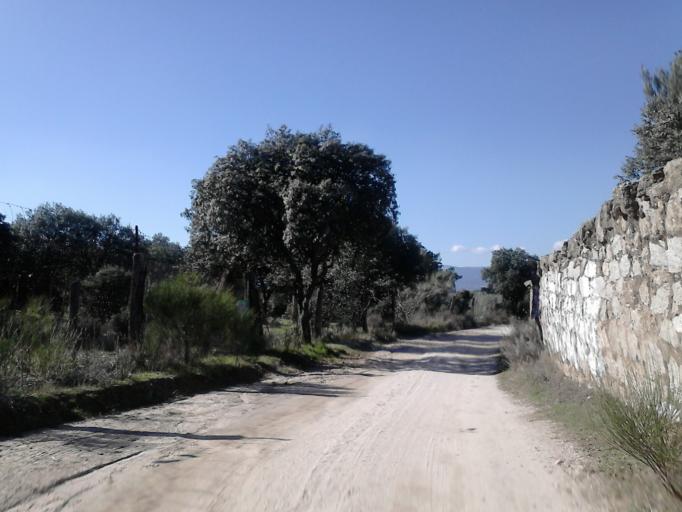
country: ES
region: Madrid
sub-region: Provincia de Madrid
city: Galapagar
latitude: 40.5612
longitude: -3.9905
